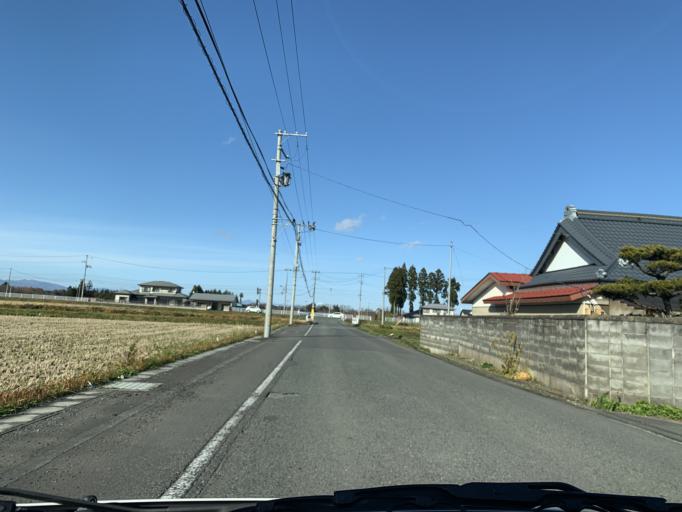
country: JP
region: Iwate
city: Mizusawa
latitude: 39.1625
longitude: 141.0990
